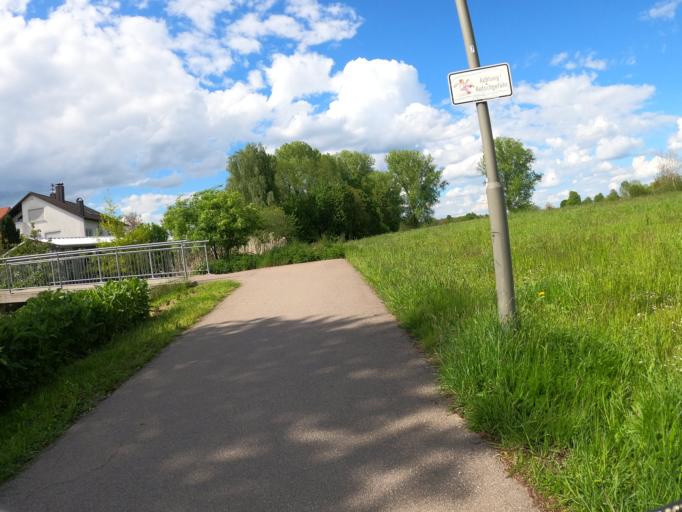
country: DE
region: Bavaria
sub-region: Swabia
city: Bubesheim
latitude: 48.4359
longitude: 10.2524
